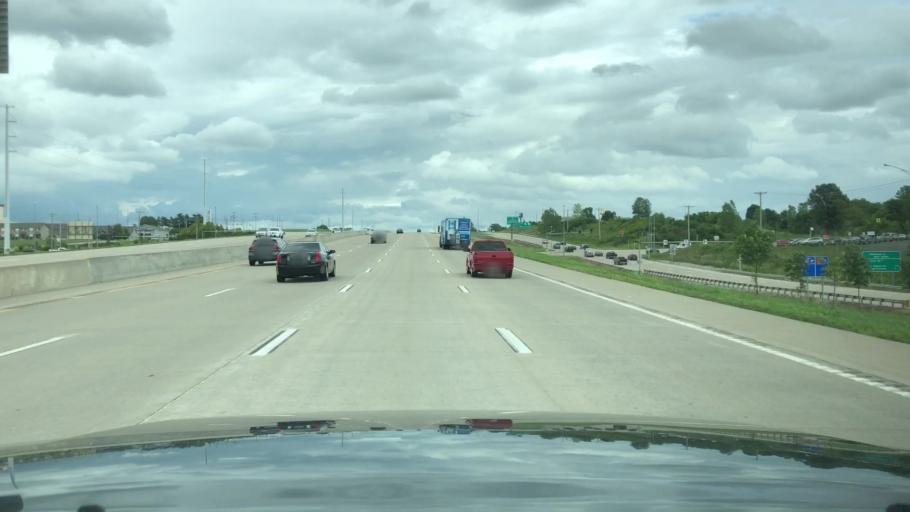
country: US
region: Missouri
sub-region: Saint Charles County
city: Saint Peters
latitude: 38.7477
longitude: -90.5868
